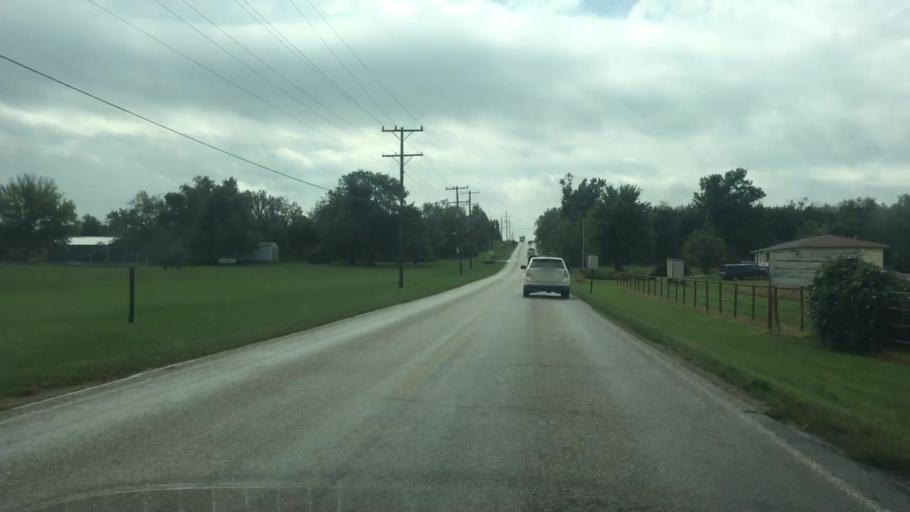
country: US
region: Kansas
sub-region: Allen County
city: Humboldt
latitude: 37.8654
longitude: -95.4369
